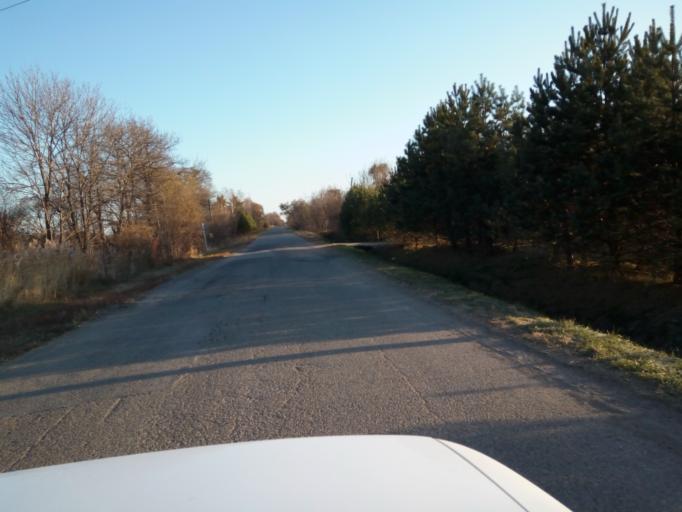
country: RU
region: Primorskiy
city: Lazo
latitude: 45.8655
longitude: 133.6432
